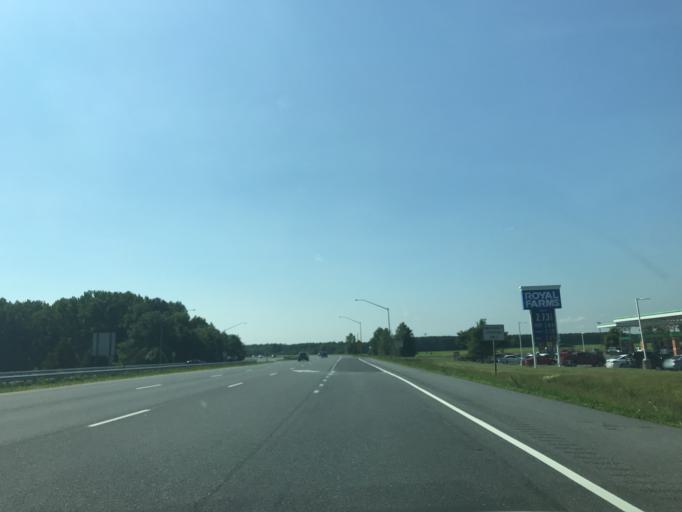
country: US
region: Maryland
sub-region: Wicomico County
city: Hebron
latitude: 38.4090
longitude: -75.6417
